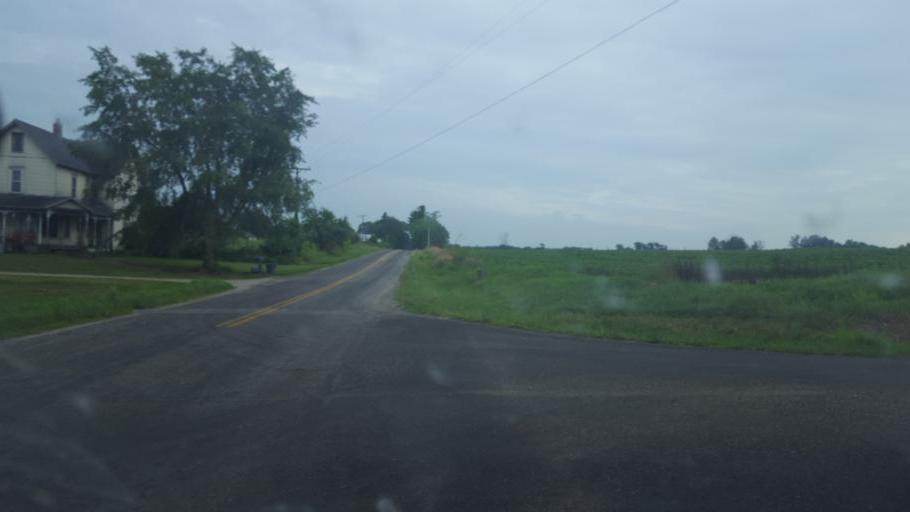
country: US
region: Ohio
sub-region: Ashland County
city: Loudonville
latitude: 40.7702
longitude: -82.1566
